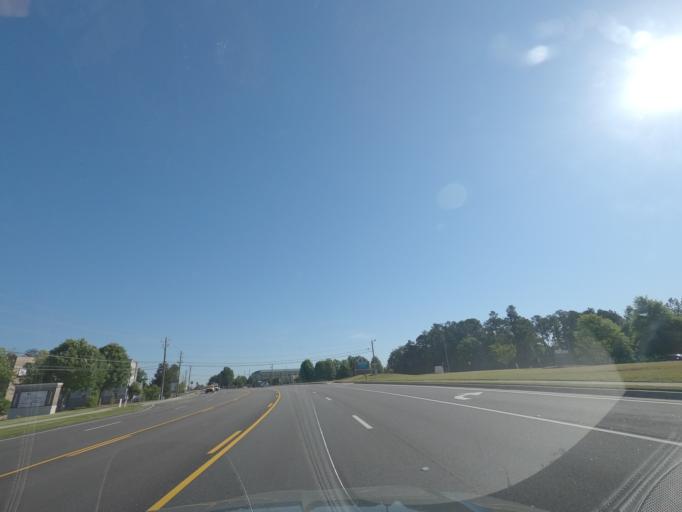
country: US
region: Georgia
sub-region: Columbia County
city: Evans
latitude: 33.5293
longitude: -82.1313
